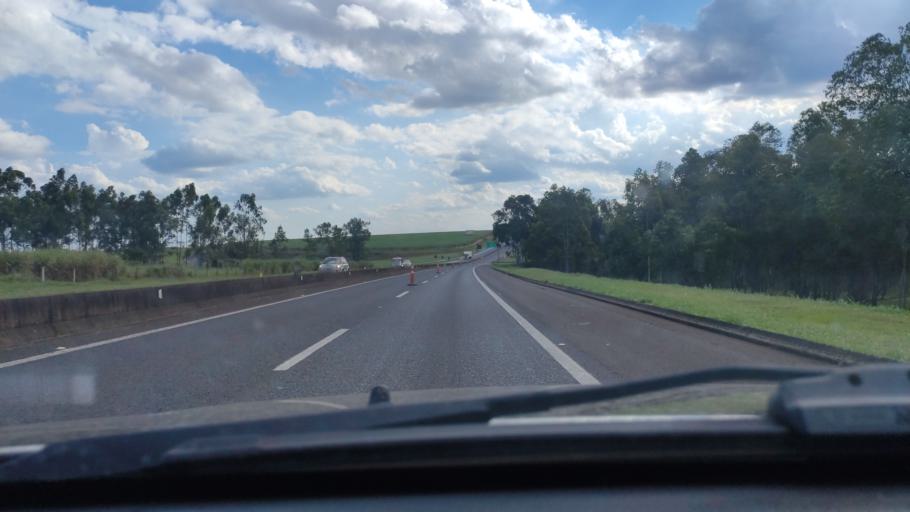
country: BR
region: Sao Paulo
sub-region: Ourinhos
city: Ourinhos
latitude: -22.9255
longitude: -49.8212
